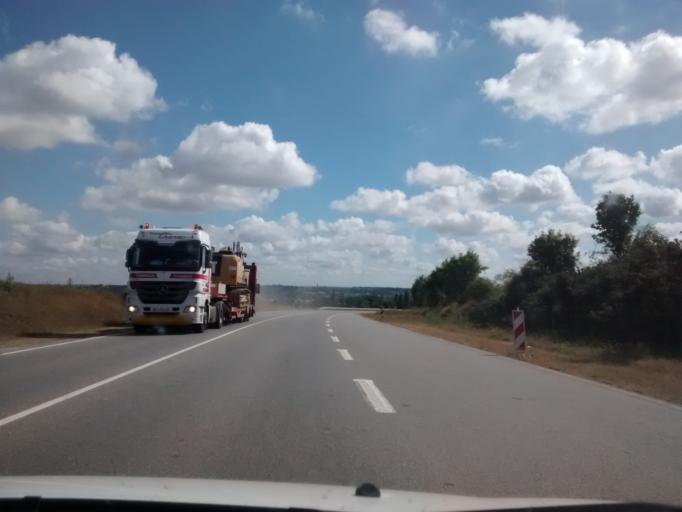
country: FR
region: Brittany
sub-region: Departement d'Ille-et-Vilaine
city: Bain-de-Bretagne
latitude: 47.8488
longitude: -1.7010
